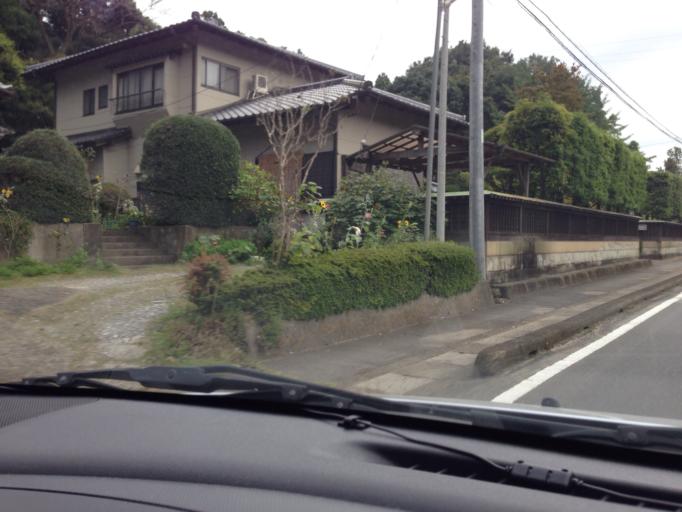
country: JP
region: Ibaraki
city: Inashiki
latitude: 36.0184
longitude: 140.2962
